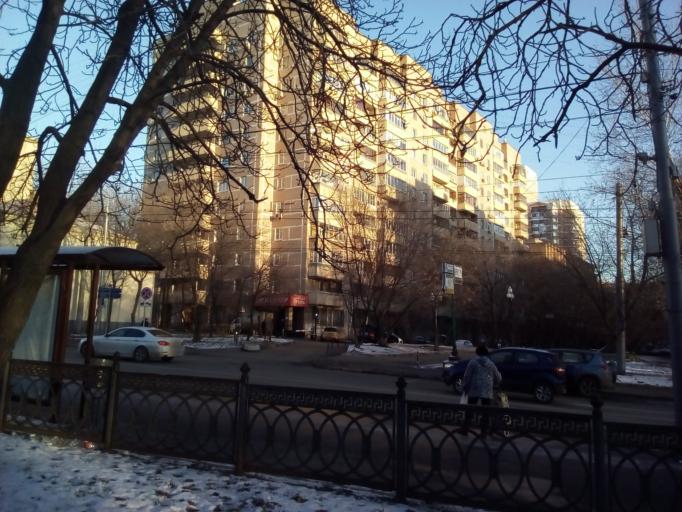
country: RU
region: Moskovskaya
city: Dorogomilovo
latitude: 55.7668
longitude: 37.5783
